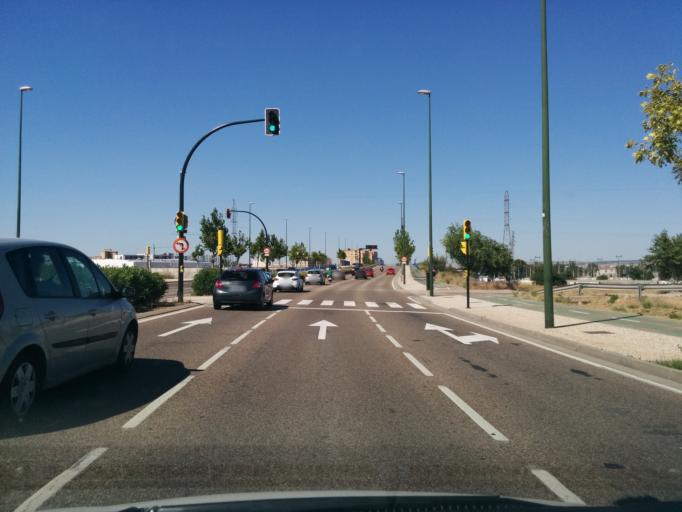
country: ES
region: Aragon
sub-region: Provincia de Zaragoza
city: Zaragoza
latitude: 41.6297
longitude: -0.8683
